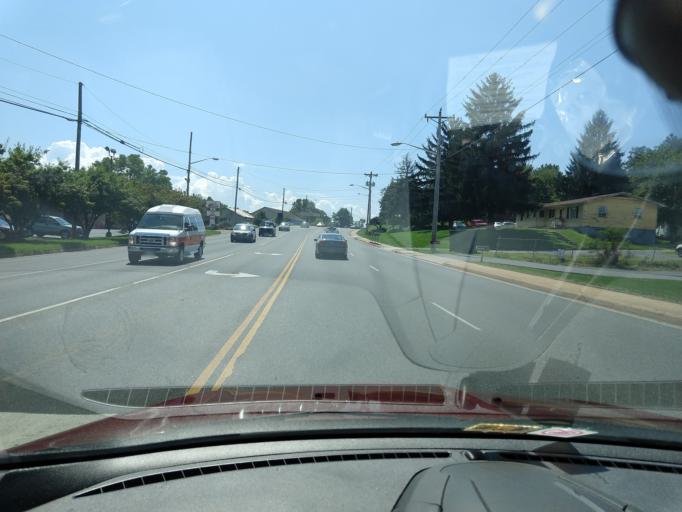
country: US
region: Virginia
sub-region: City of Harrisonburg
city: Harrisonburg
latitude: 38.4684
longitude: -78.8714
